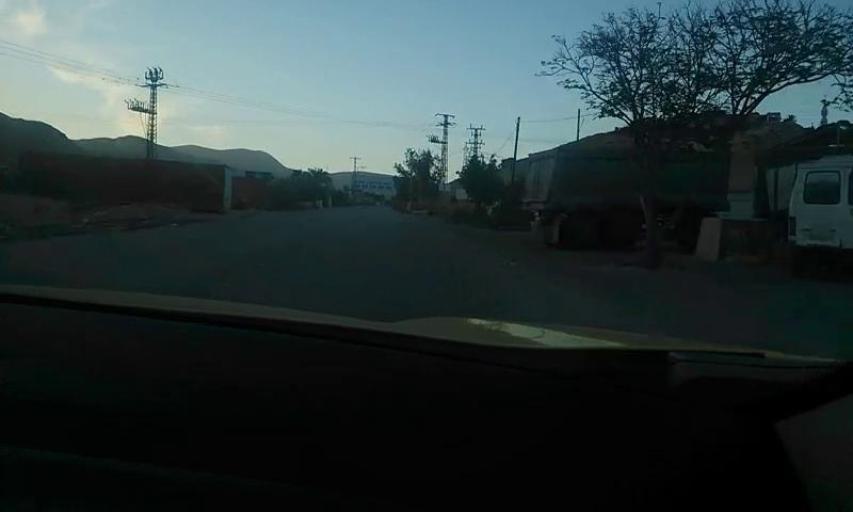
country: PS
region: West Bank
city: An Nuway`imah
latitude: 31.8942
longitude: 35.4290
